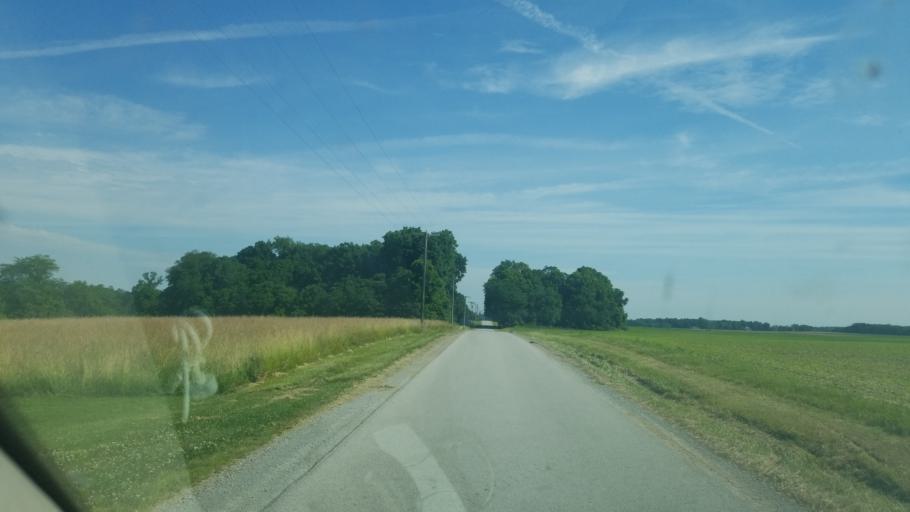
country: US
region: Ohio
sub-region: Wyandot County
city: Upper Sandusky
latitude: 40.8497
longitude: -83.2369
